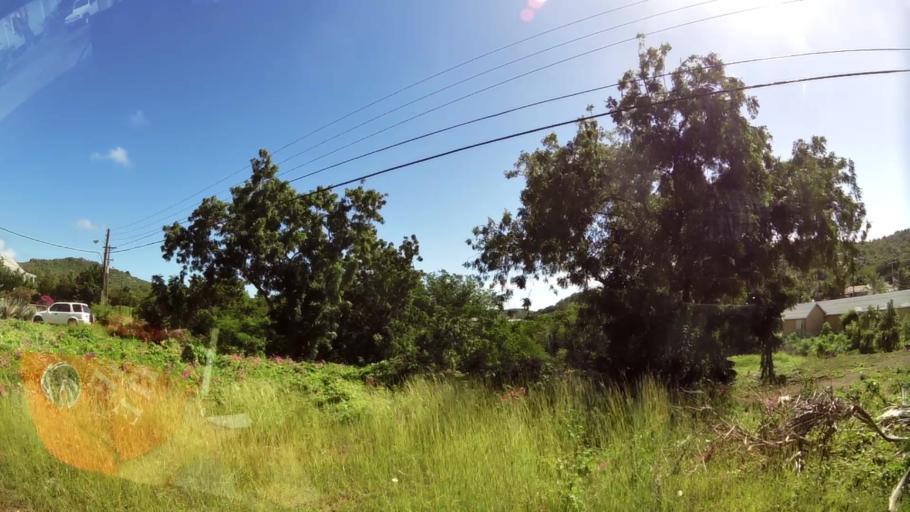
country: AG
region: Saint Paul
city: Falmouth
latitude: 17.0116
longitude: -61.7678
